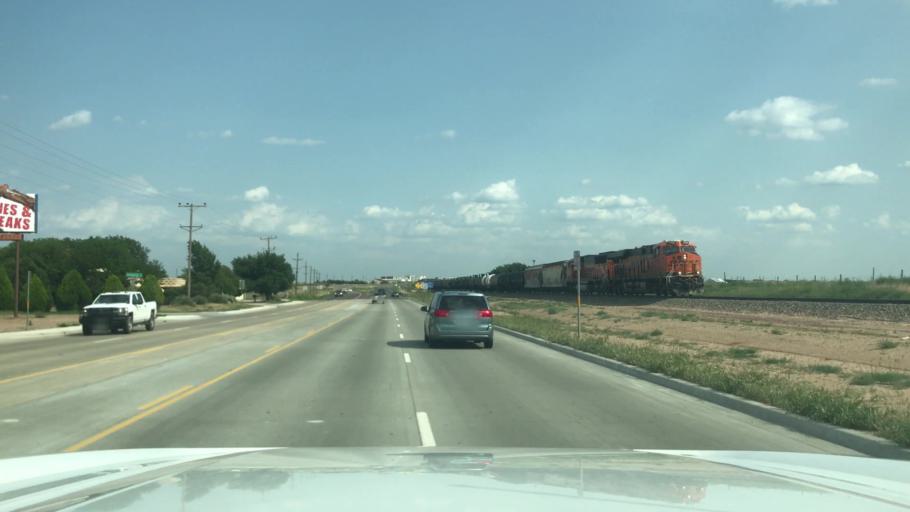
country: US
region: Texas
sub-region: Dallam County
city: Dalhart
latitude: 36.0486
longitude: -102.4973
